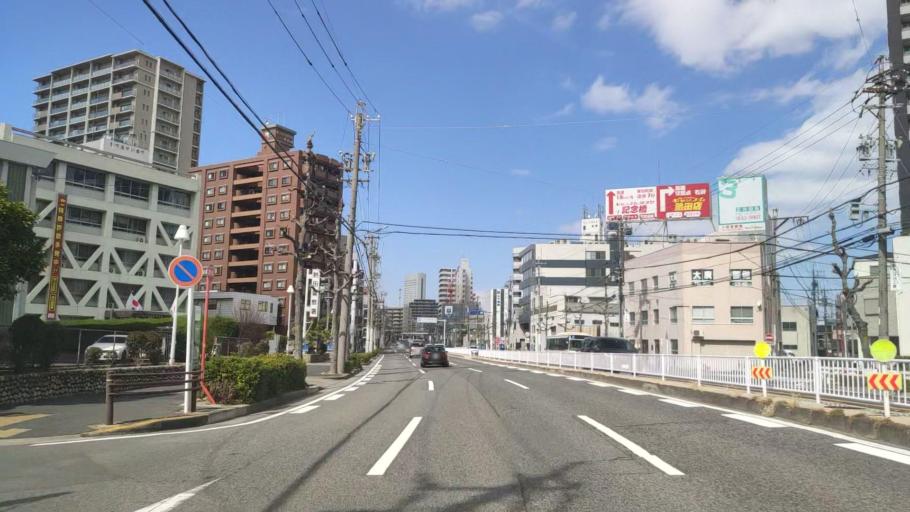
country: JP
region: Aichi
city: Nagoya-shi
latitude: 35.1328
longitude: 136.9080
